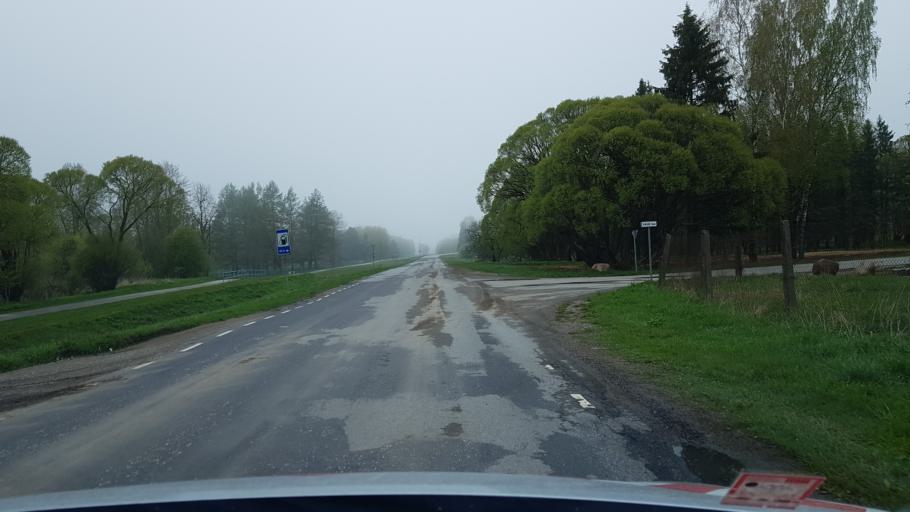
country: EE
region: Harju
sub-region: Joelaehtme vald
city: Loo
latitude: 59.4297
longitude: 24.9423
